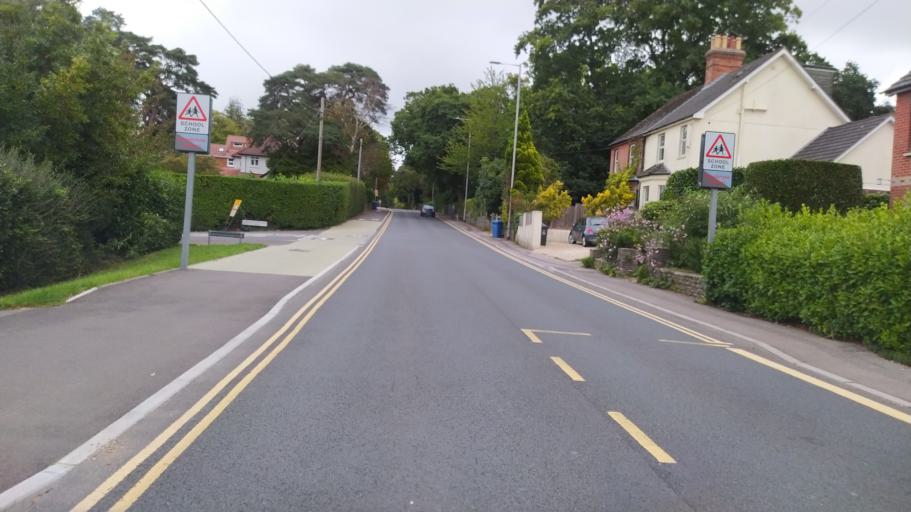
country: GB
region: England
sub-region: Dorset
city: Broadstone
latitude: 50.7630
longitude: -1.9896
